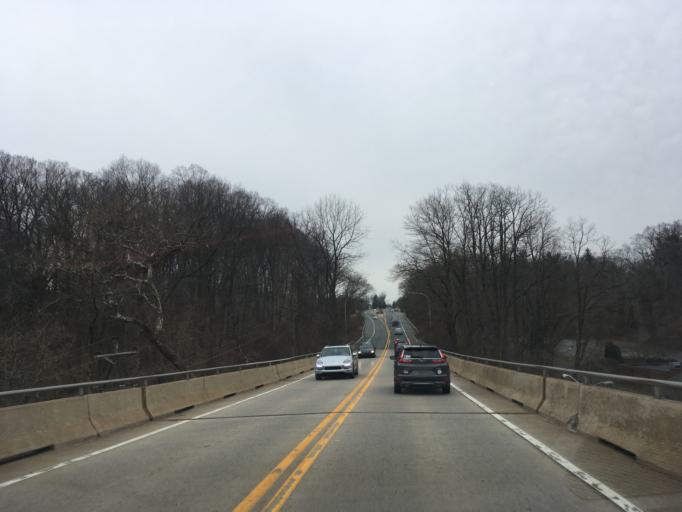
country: US
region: Delaware
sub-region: New Castle County
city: Greenville
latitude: 39.7732
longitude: -75.5788
